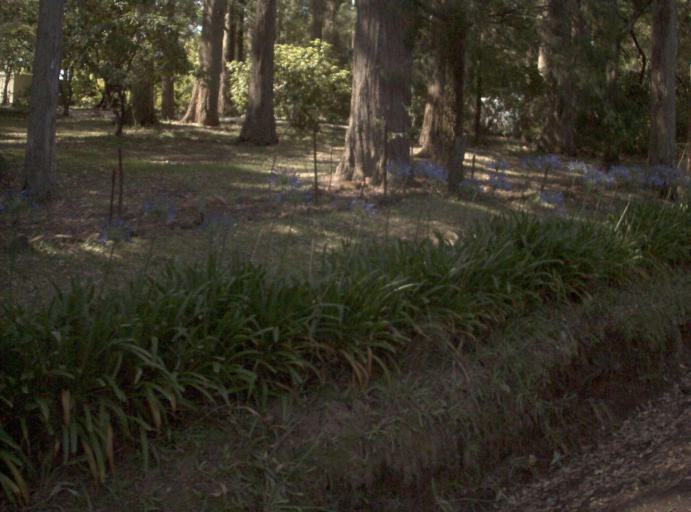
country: AU
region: Victoria
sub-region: Yarra Ranges
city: Mount Dandenong
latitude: -37.8328
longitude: 145.3515
